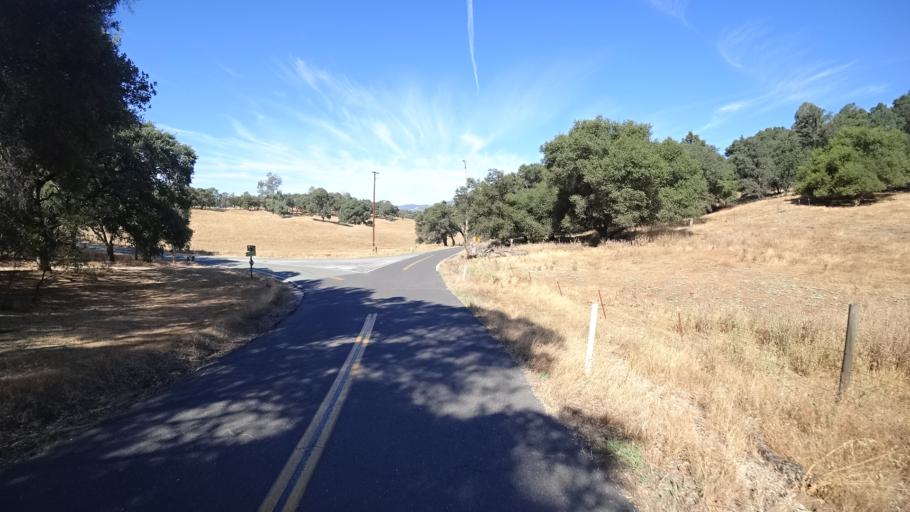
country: US
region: California
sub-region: Calaveras County
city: San Andreas
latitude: 38.1520
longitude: -120.5975
